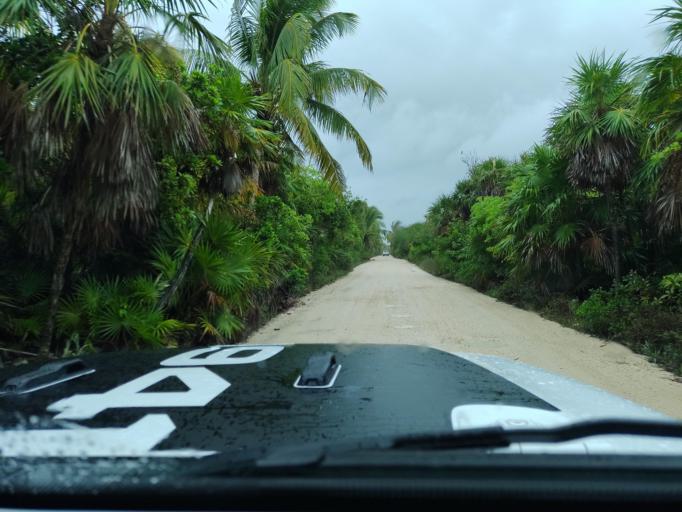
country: MX
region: Quintana Roo
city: Tulum
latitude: 19.9893
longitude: -87.4651
